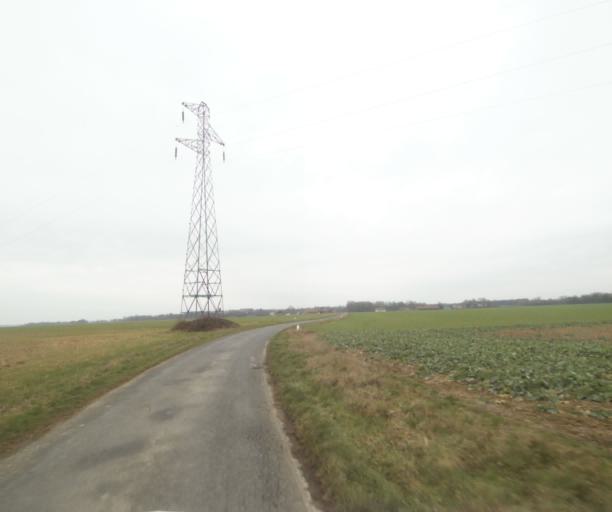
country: FR
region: Champagne-Ardenne
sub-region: Departement de la Haute-Marne
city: Villiers-en-Lieu
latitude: 48.6326
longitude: 4.8230
